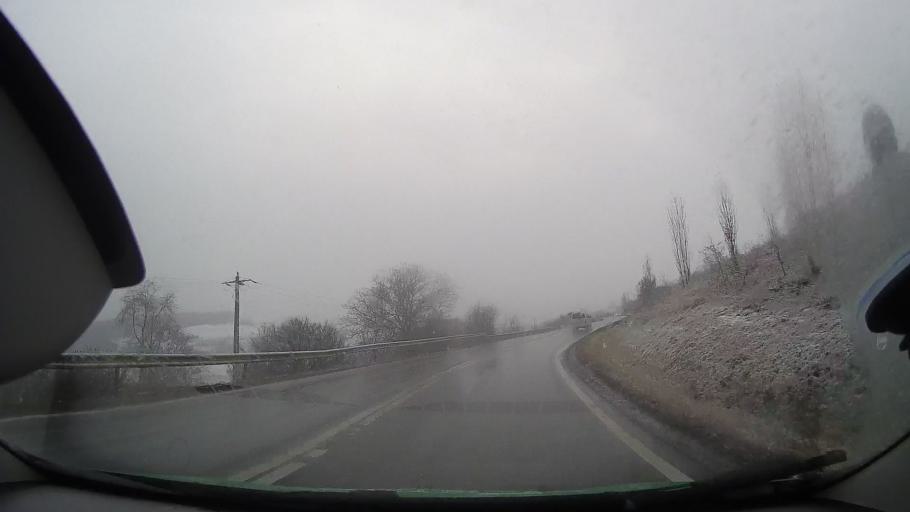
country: RO
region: Mures
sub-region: Comuna Bagaciu
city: Delenii
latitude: 46.2621
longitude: 24.3021
